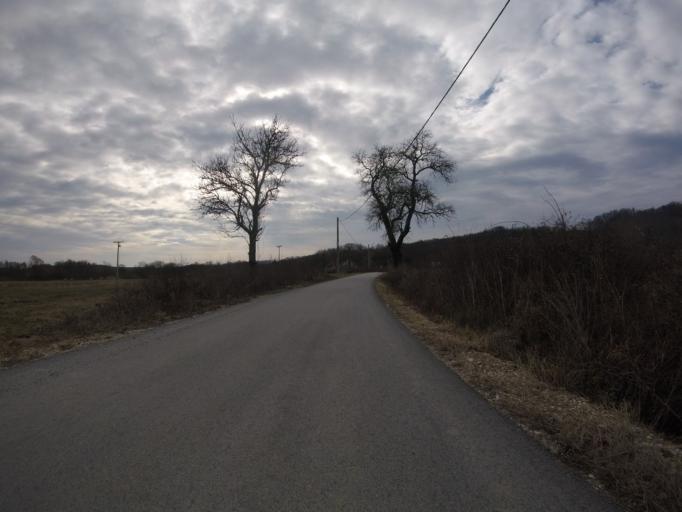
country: HR
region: Sisacko-Moslavacka
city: Glina
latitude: 45.4396
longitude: 16.0747
